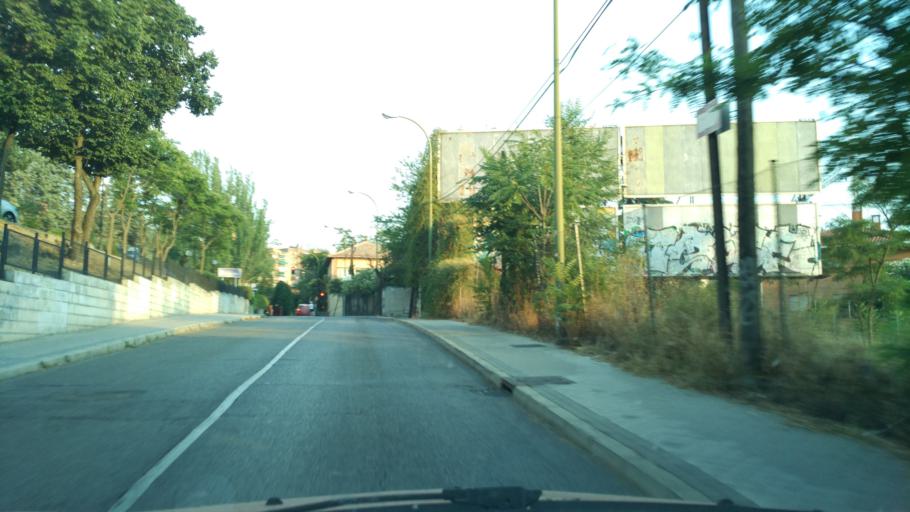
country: ES
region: Madrid
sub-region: Provincia de Madrid
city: Tetuan de las Victorias
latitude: 40.4688
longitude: -3.7253
